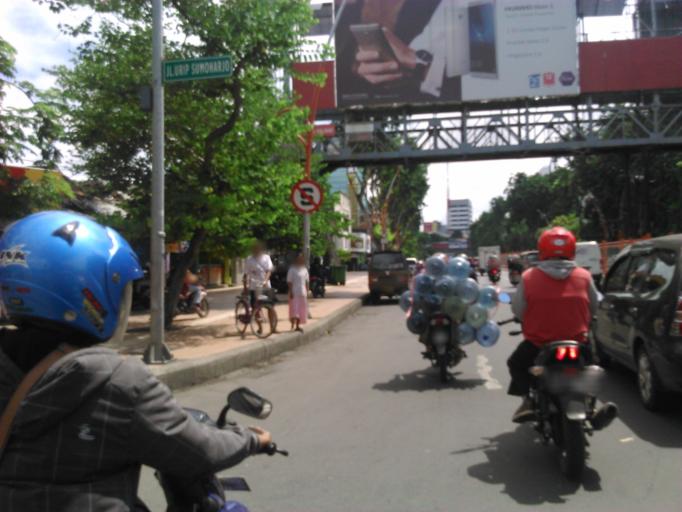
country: ID
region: East Java
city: Gubengairlangga
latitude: -7.2773
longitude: 112.7412
